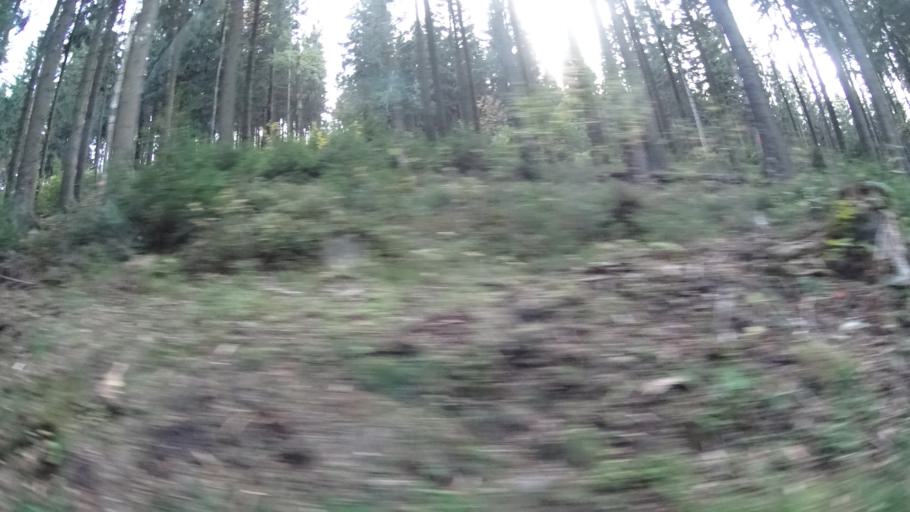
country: DE
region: Thuringia
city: Bermbach
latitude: 50.6872
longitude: 10.6425
